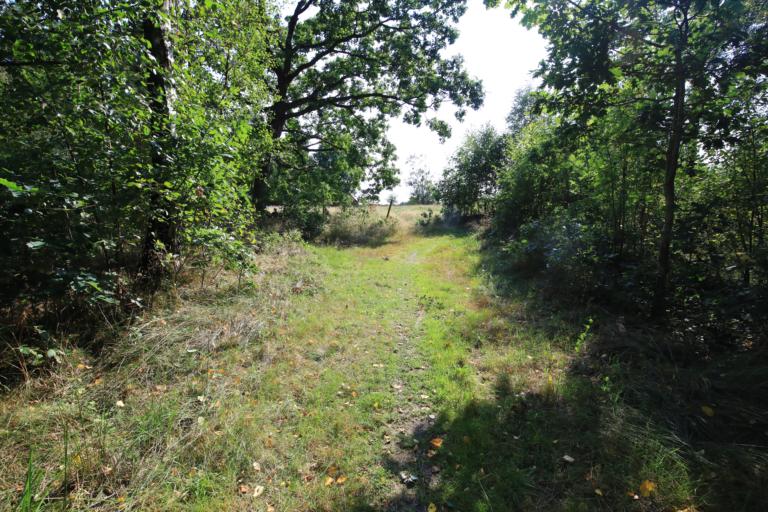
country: SE
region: Halland
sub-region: Varbergs Kommun
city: Varberg
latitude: 57.1756
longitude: 12.2167
